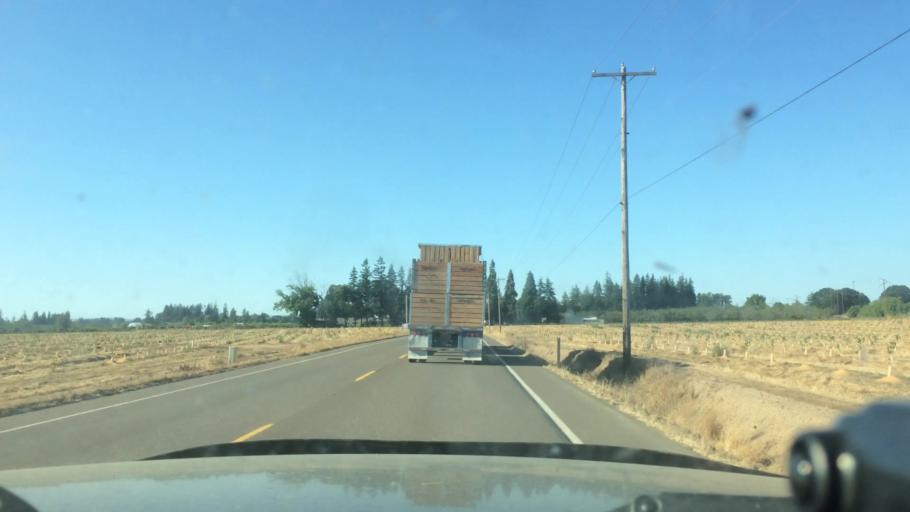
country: US
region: Oregon
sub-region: Marion County
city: Hayesville
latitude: 45.0655
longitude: -122.9806
